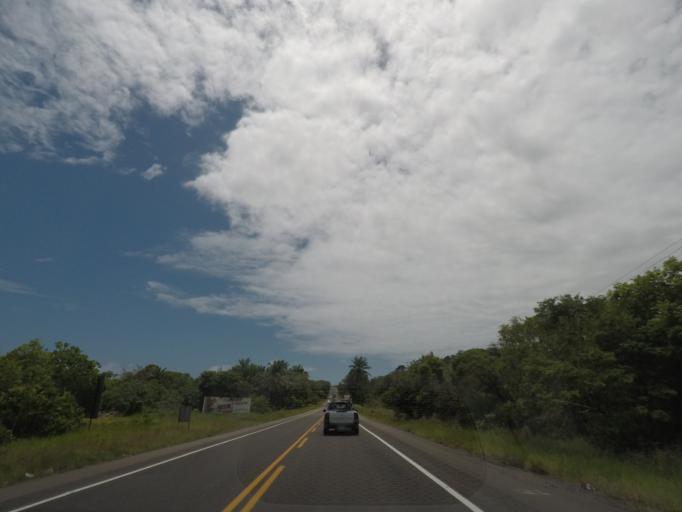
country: BR
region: Bahia
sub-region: Itaparica
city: Itaparica
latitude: -12.9679
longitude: -38.6358
